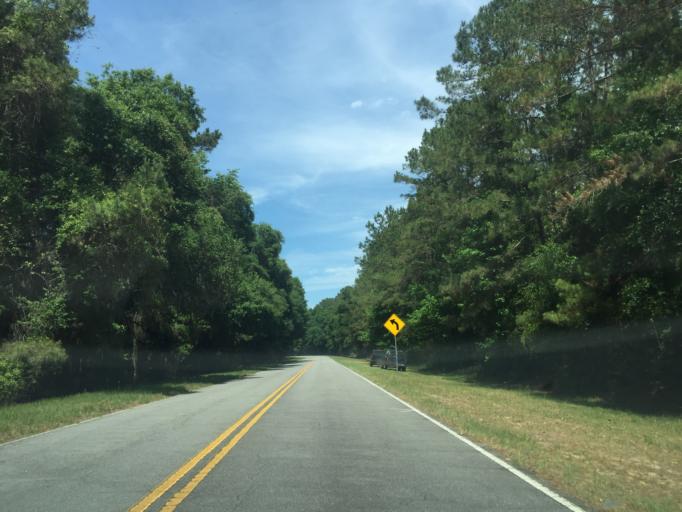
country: US
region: Georgia
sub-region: Chatham County
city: Isle of Hope
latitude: 31.9706
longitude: -81.0309
